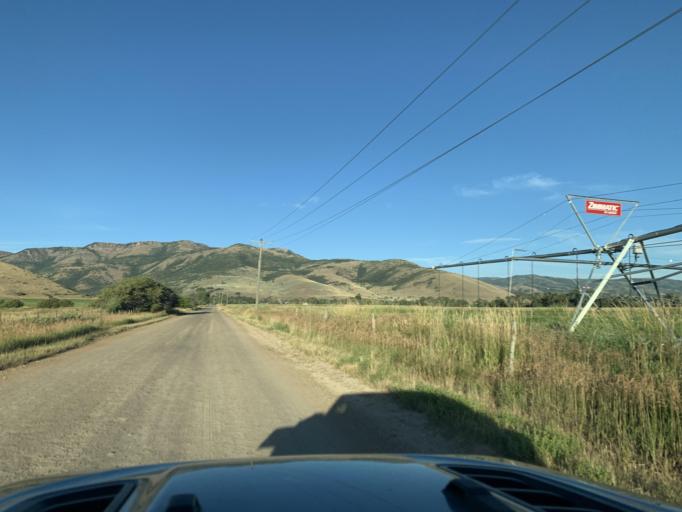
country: US
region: Utah
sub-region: Weber County
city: Wolf Creek
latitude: 41.2931
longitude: -111.7735
